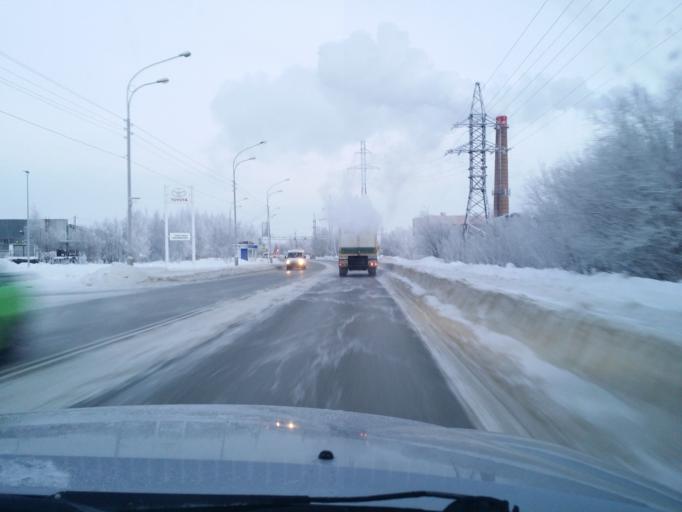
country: RU
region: Khanty-Mansiyskiy Avtonomnyy Okrug
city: Nizhnevartovsk
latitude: 60.9483
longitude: 76.5226
